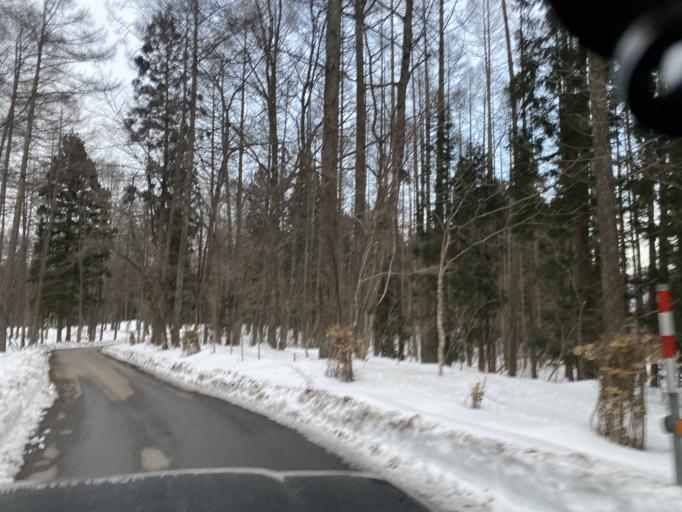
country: JP
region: Nagano
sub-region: Kitaazumi Gun
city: Hakuba
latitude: 36.7140
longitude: 137.8599
